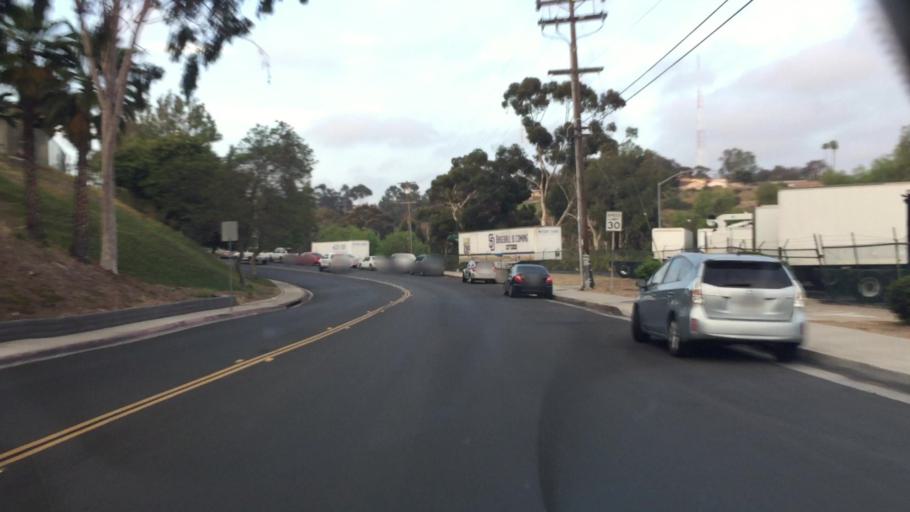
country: US
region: California
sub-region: San Diego County
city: National City
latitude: 32.7216
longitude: -117.0807
